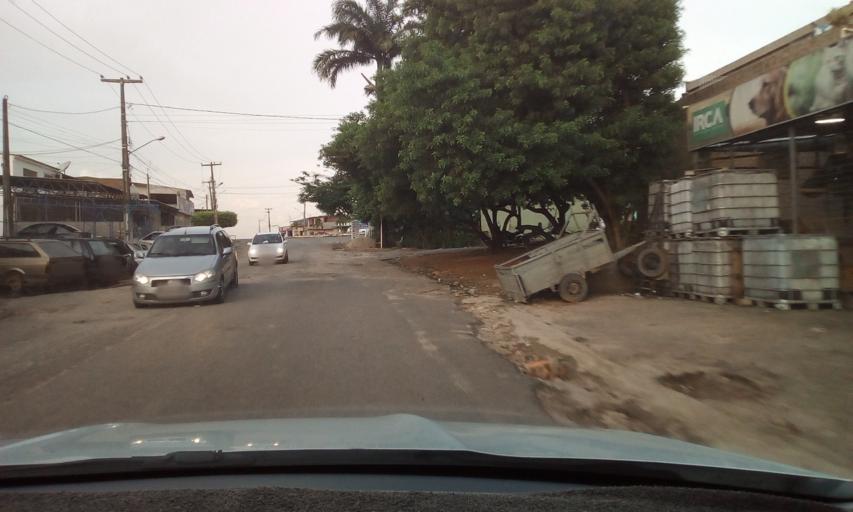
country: BR
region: Pernambuco
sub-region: Vicencia
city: Vicencia
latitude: -7.5983
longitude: -35.2318
